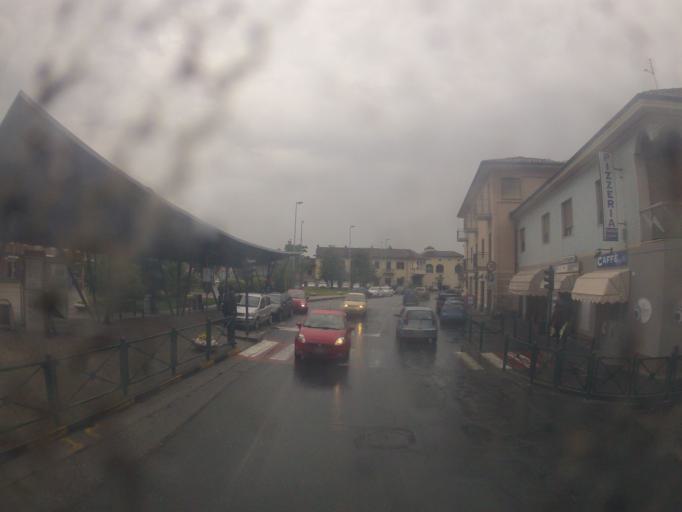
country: IT
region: Piedmont
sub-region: Provincia di Torino
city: La Loggia
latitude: 44.9568
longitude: 7.6673
